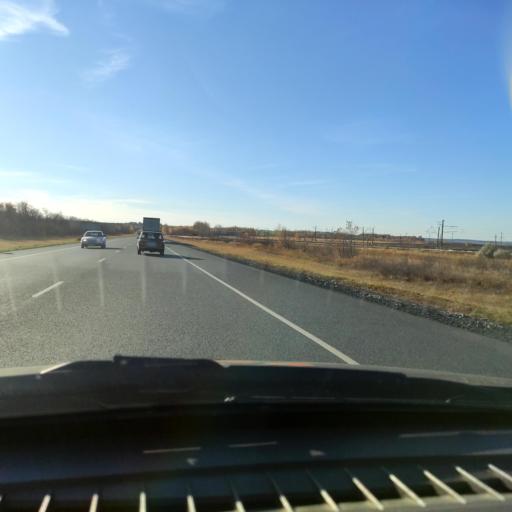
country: RU
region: Samara
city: Obsharovka
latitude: 53.2368
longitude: 48.9495
